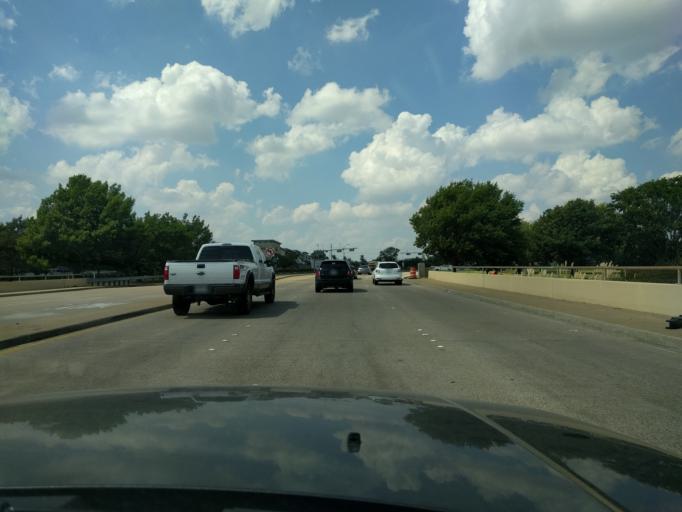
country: US
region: Texas
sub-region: Collin County
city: Allen
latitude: 33.0662
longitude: -96.6903
